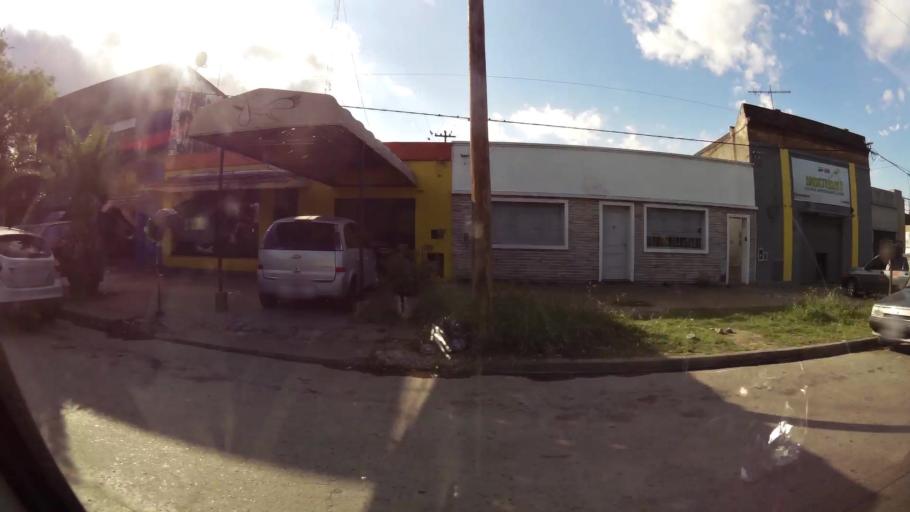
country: AR
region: Buenos Aires
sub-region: Partido de La Plata
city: La Plata
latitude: -34.8915
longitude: -57.9599
